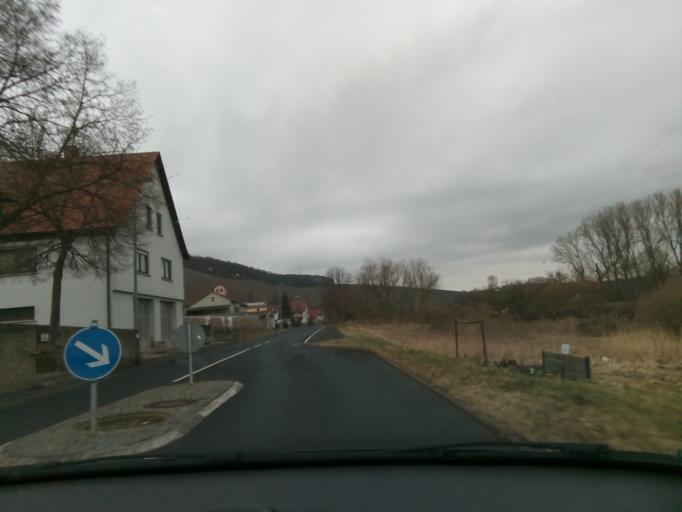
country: DE
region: Bavaria
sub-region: Regierungsbezirk Unterfranken
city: Nordheim
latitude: 49.8461
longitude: 10.1685
